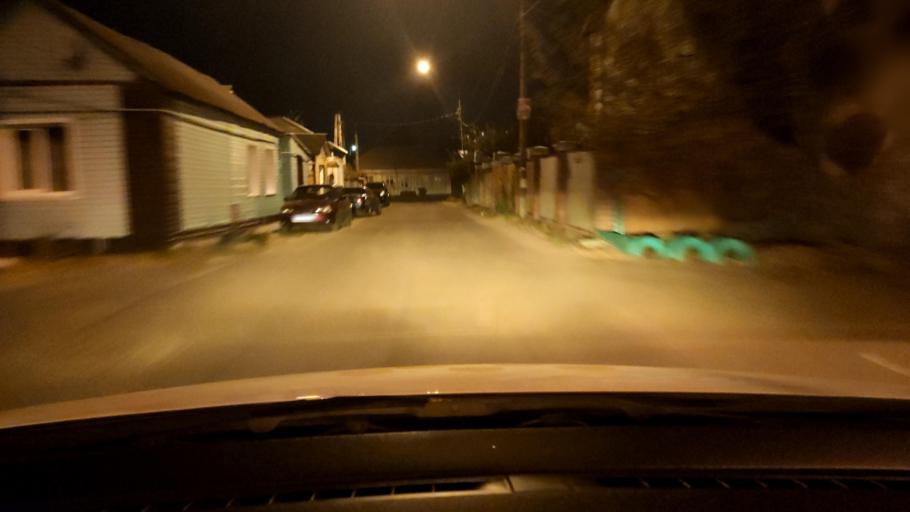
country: RU
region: Voronezj
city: Voronezh
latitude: 51.6648
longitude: 39.1660
